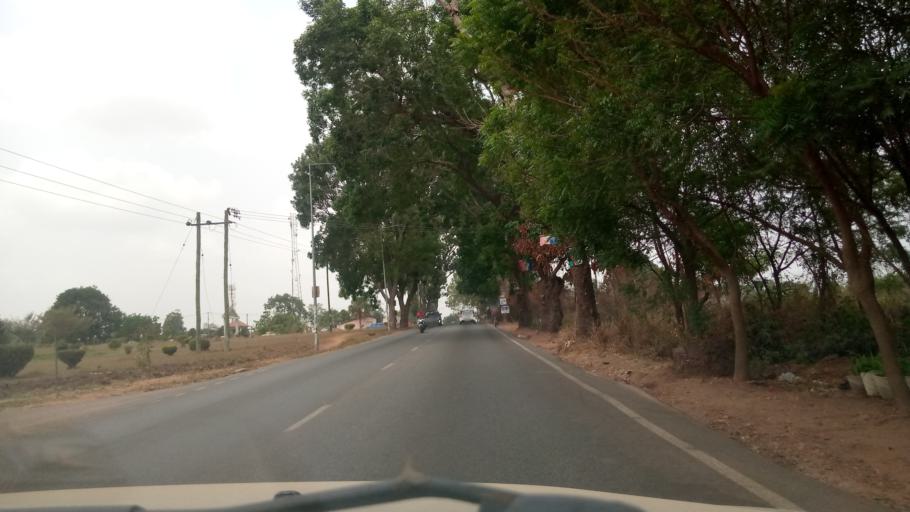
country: GH
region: Greater Accra
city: Dome
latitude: 5.6677
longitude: -0.2297
